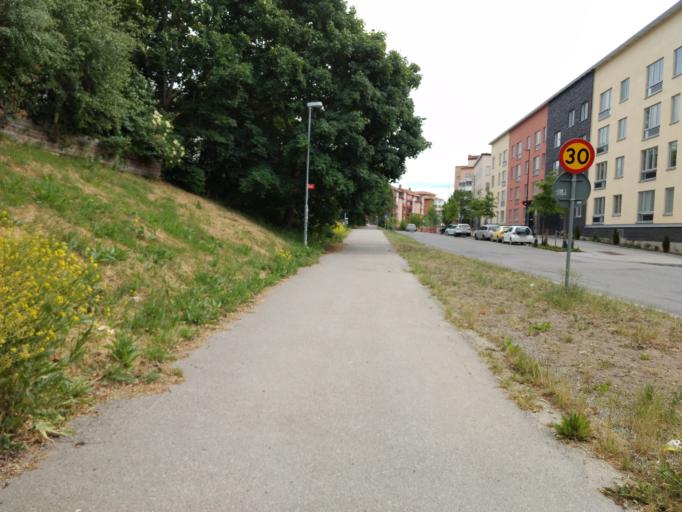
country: SE
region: Stockholm
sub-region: Upplands Vasby Kommun
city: Upplands Vaesby
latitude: 59.5240
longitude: 17.9041
